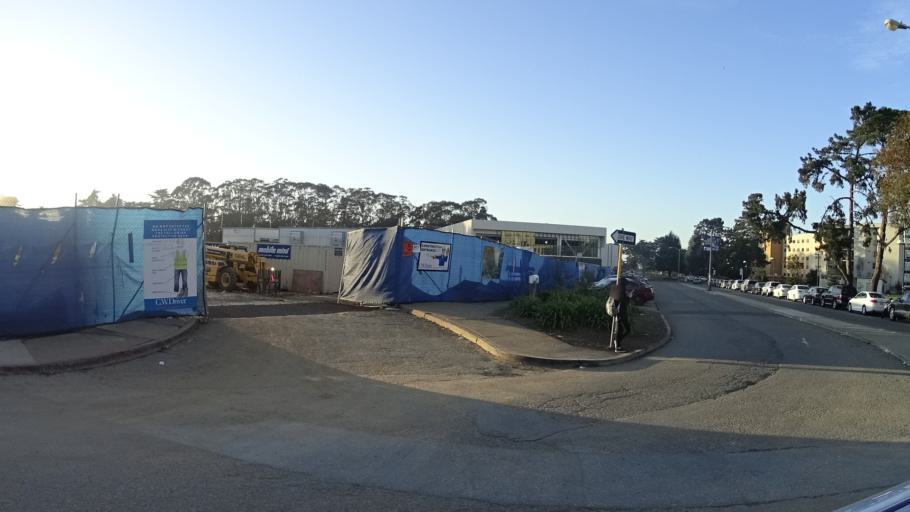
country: US
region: California
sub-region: San Mateo County
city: Daly City
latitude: 37.7218
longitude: -122.4825
